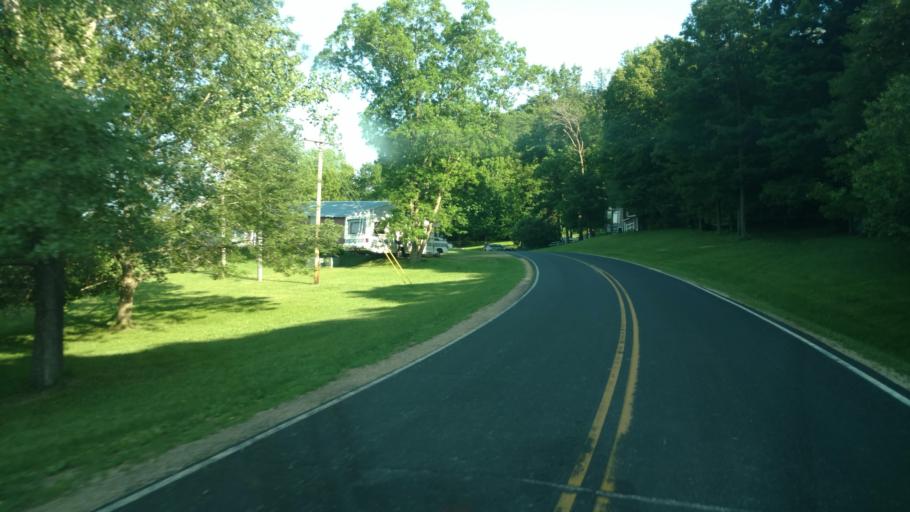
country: US
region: Wisconsin
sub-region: Vernon County
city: Hillsboro
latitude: 43.6732
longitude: -90.3527
